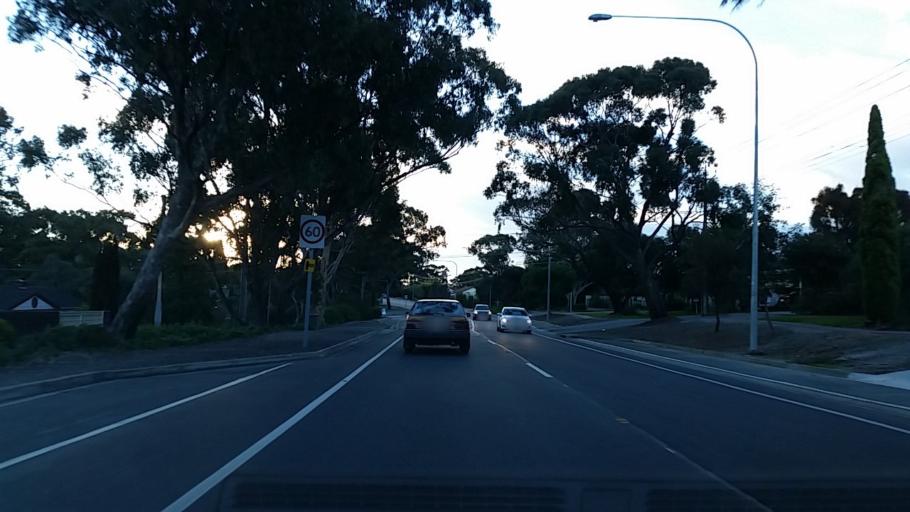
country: AU
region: South Australia
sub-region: Onkaparinga
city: Craigburn Farm
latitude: -35.0530
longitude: 138.5931
